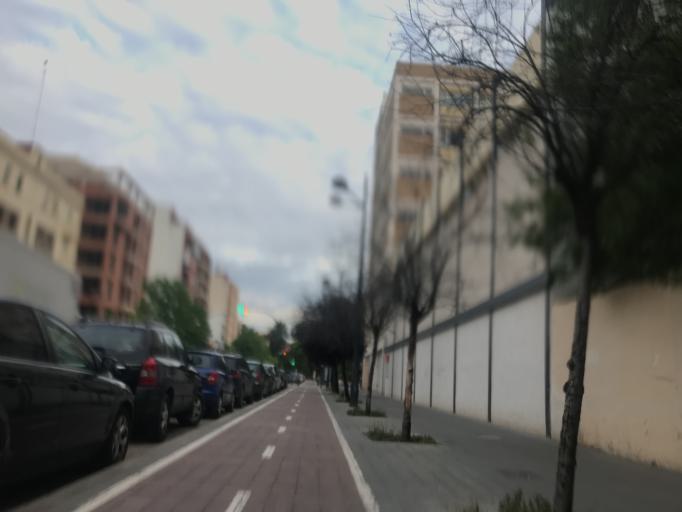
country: ES
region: Valencia
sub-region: Provincia de Valencia
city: Alboraya
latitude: 39.4658
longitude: -0.3417
